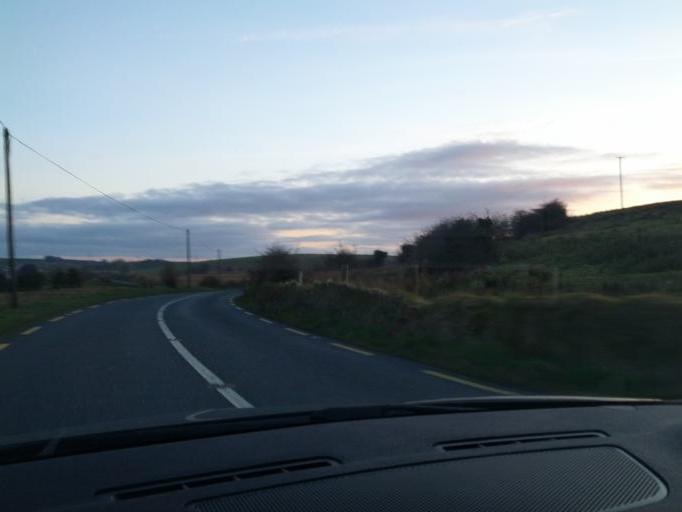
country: IE
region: Connaught
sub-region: Roscommon
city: Boyle
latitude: 53.9406
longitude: -8.2736
